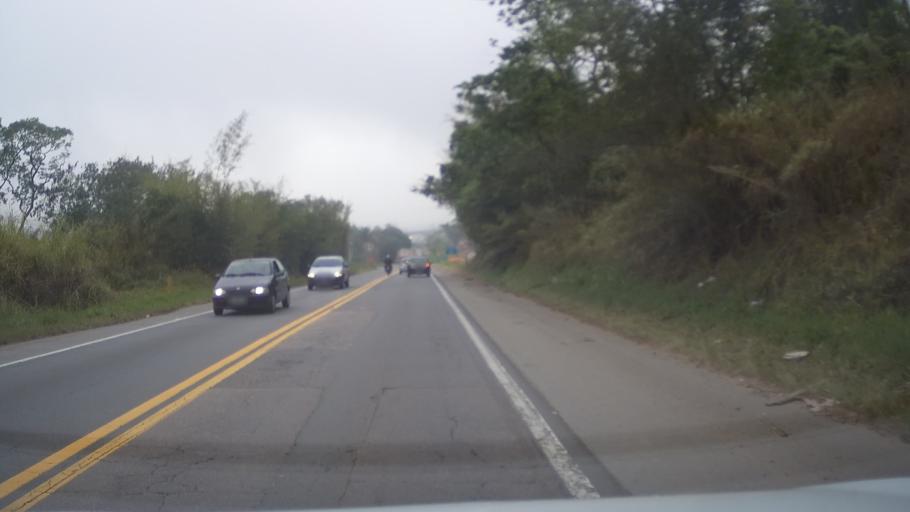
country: BR
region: Sao Paulo
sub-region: Itatiba
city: Itatiba
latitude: -22.9948
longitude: -46.8023
